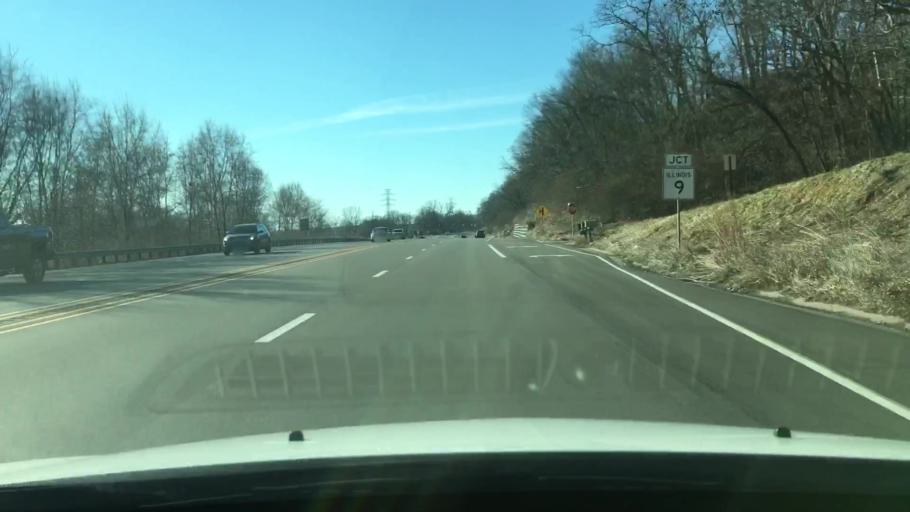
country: US
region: Illinois
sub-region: Tazewell County
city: Pekin
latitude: 40.5920
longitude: -89.6754
